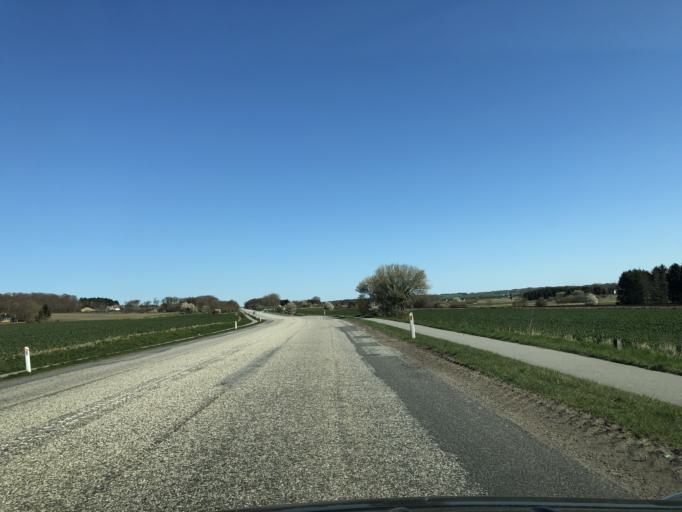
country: DK
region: North Denmark
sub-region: Rebild Kommune
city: Stovring
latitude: 56.9196
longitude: 9.8584
